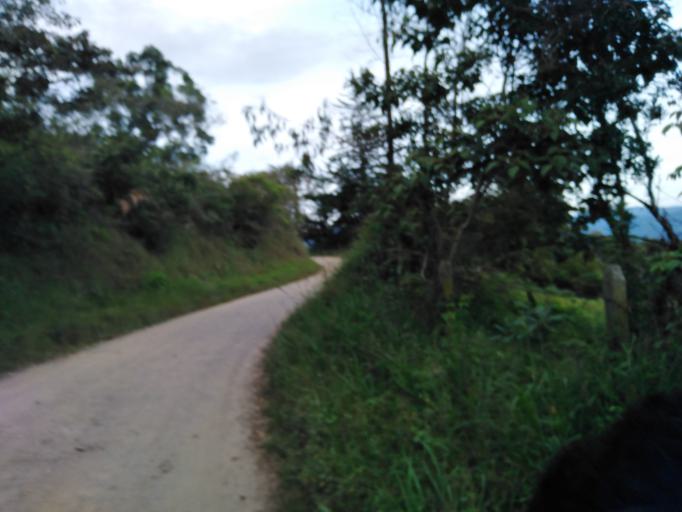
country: CO
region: Cundinamarca
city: Tenza
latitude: 5.1040
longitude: -73.4154
